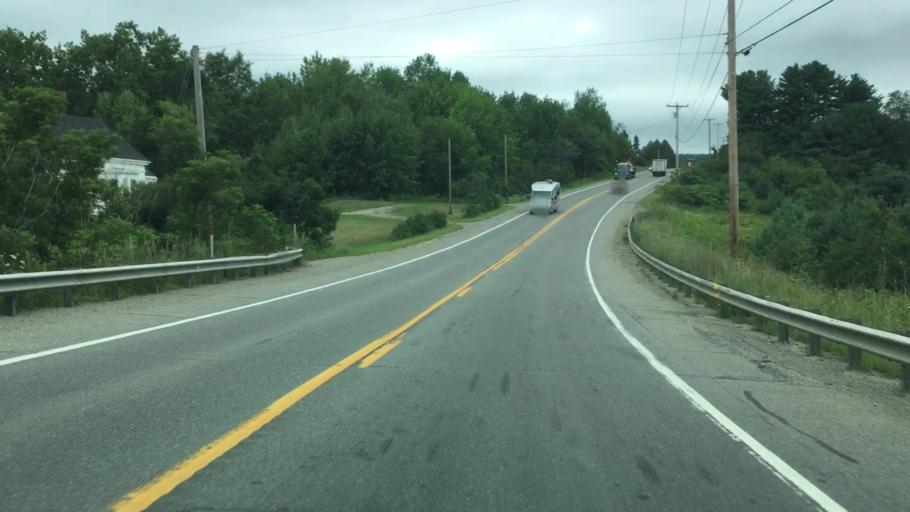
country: US
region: Maine
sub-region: Waldo County
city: Frankfort
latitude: 44.5584
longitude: -68.8660
